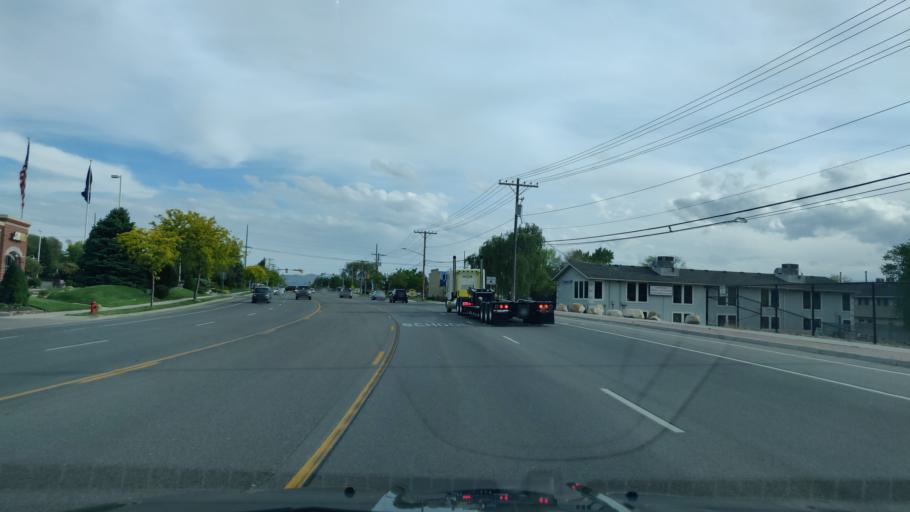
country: US
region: Utah
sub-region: Salt Lake County
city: Sandy City
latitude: 40.6116
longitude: -111.8721
